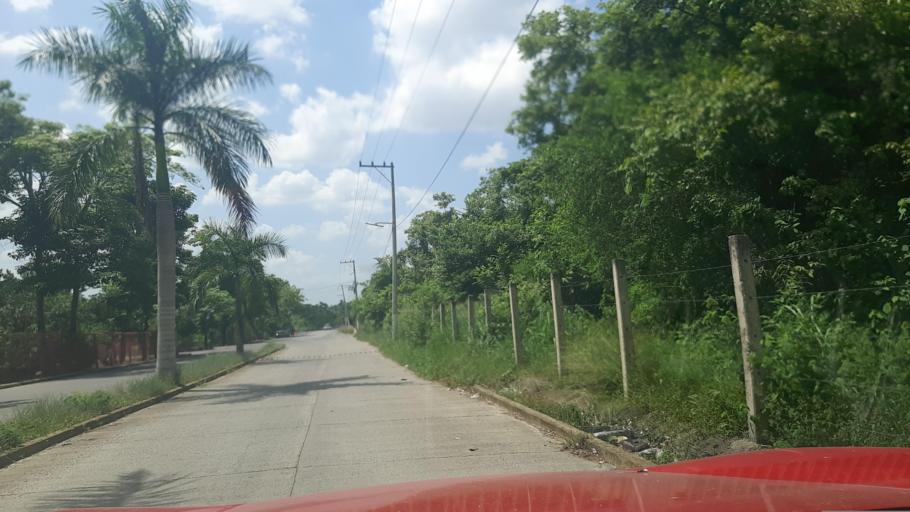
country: MX
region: Veracruz
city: Coatzintla
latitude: 20.4981
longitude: -97.4380
